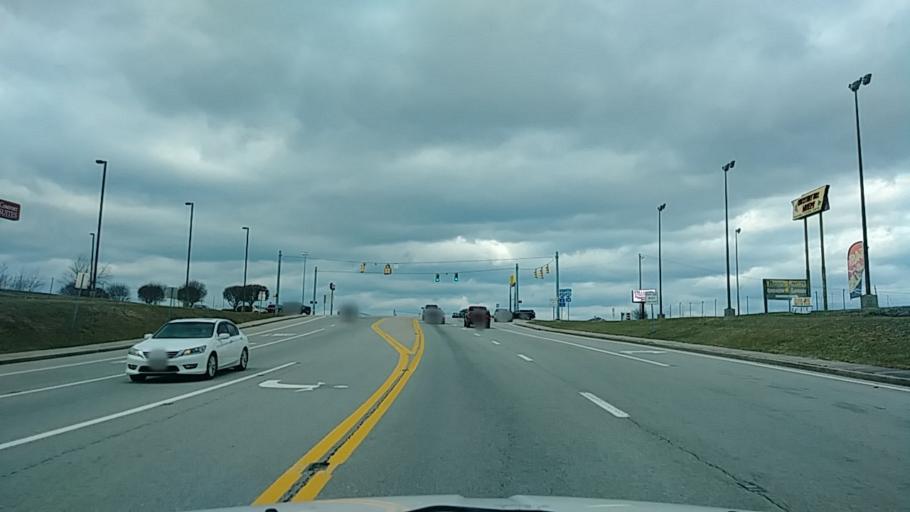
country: US
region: Tennessee
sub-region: Cumberland County
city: Crossville
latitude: 35.9608
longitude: -84.9839
